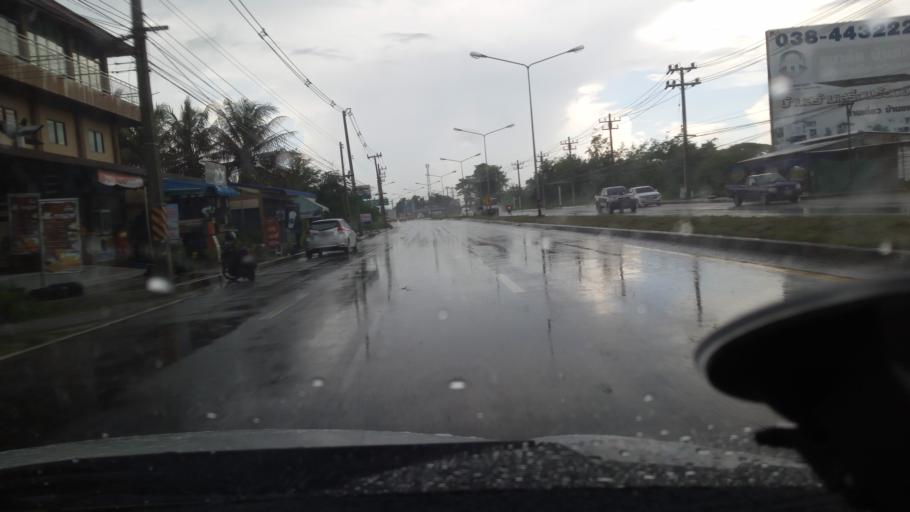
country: TH
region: Chon Buri
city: Phan Thong
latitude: 13.4288
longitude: 101.1092
